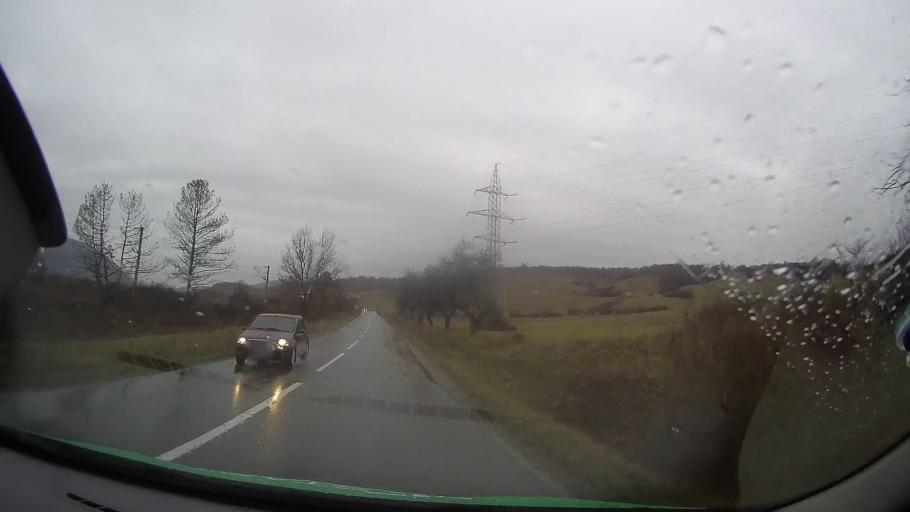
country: RO
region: Bistrita-Nasaud
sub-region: Municipiul Bistrita
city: Viisoara
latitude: 47.0458
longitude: 24.4647
